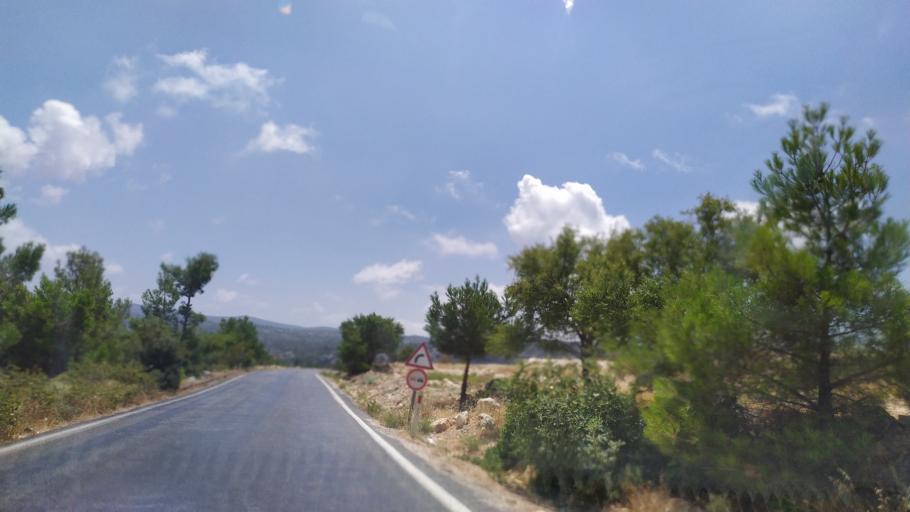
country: TR
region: Mersin
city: Gulnar
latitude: 36.2813
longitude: 33.3887
